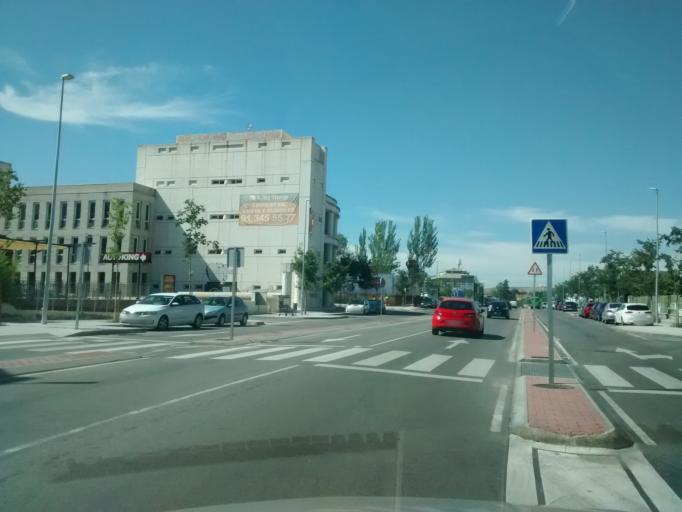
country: ES
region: Madrid
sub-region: Provincia de Madrid
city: San Fernando de Henares
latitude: 40.4328
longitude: -3.5331
